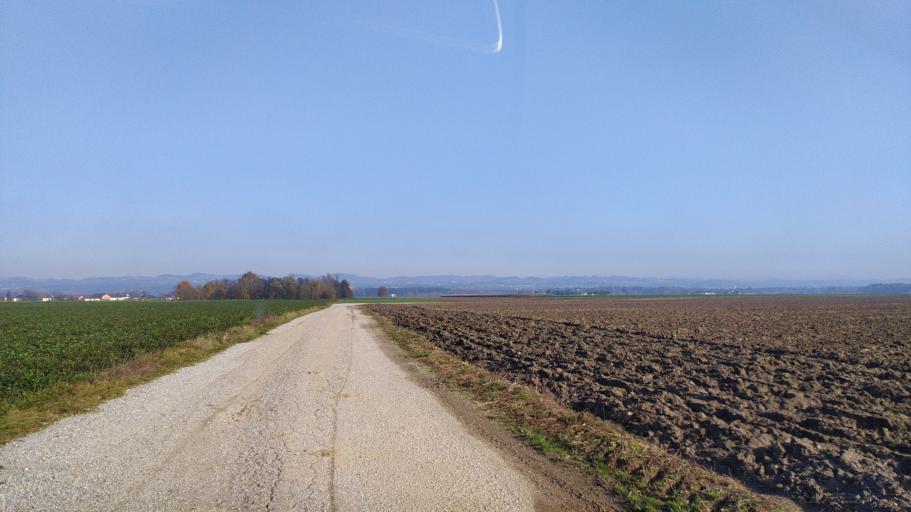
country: AT
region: Upper Austria
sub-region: Politischer Bezirk Perg
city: Perg
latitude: 48.2009
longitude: 14.6432
